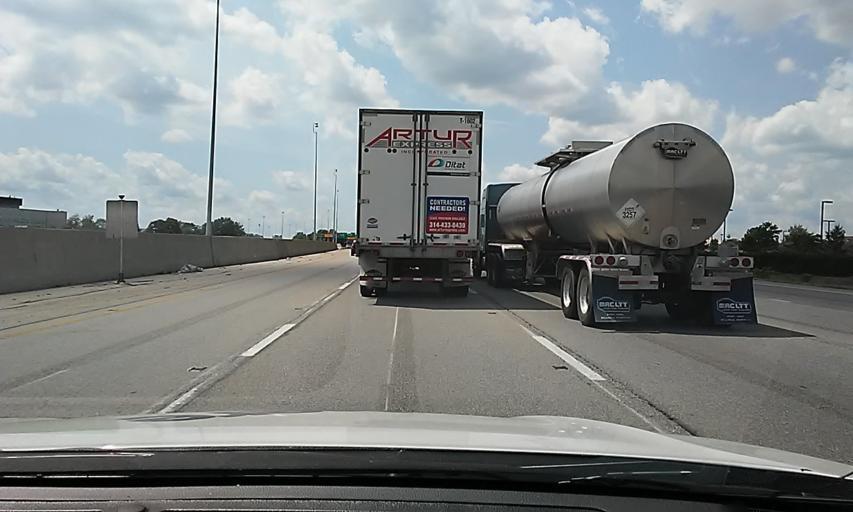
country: US
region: Ohio
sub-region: Franklin County
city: Dublin
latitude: 40.1068
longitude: -83.1233
